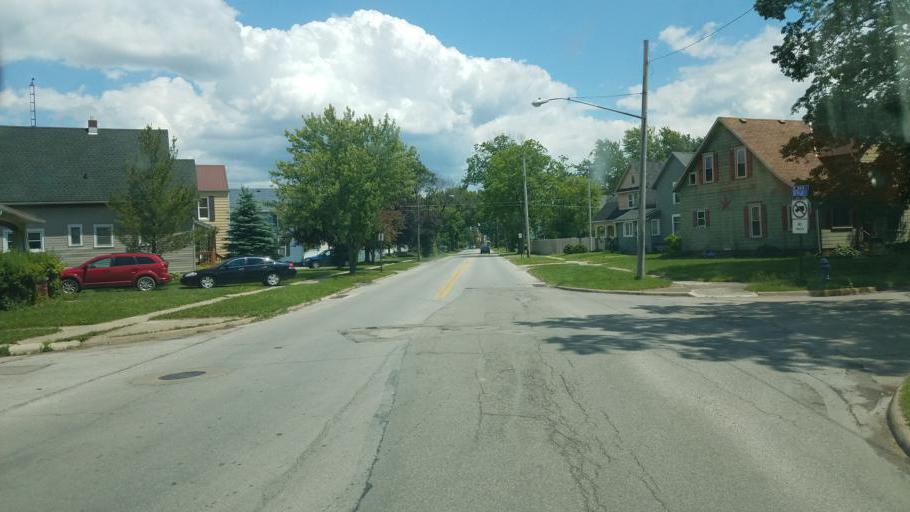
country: US
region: Ohio
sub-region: Crawford County
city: Crestline
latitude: 40.7901
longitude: -82.7438
